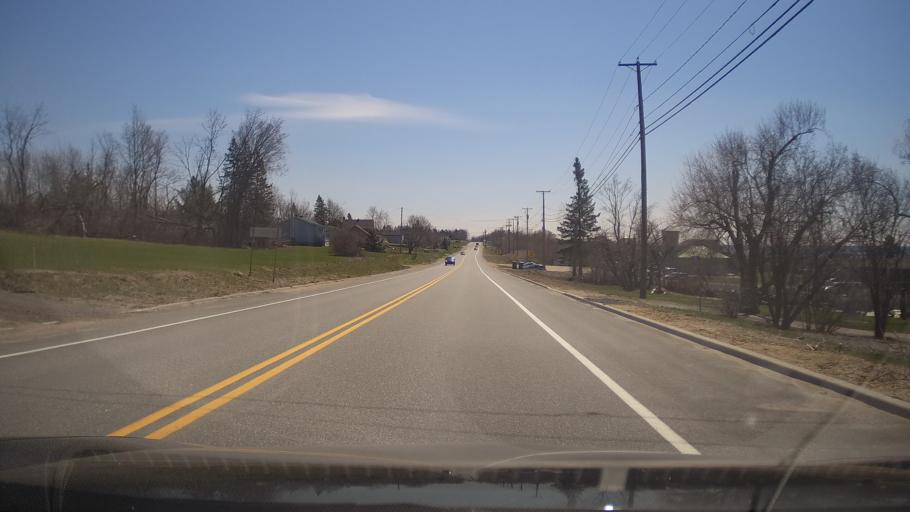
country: CA
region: Ontario
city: Bells Corners
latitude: 45.4331
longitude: -75.9053
